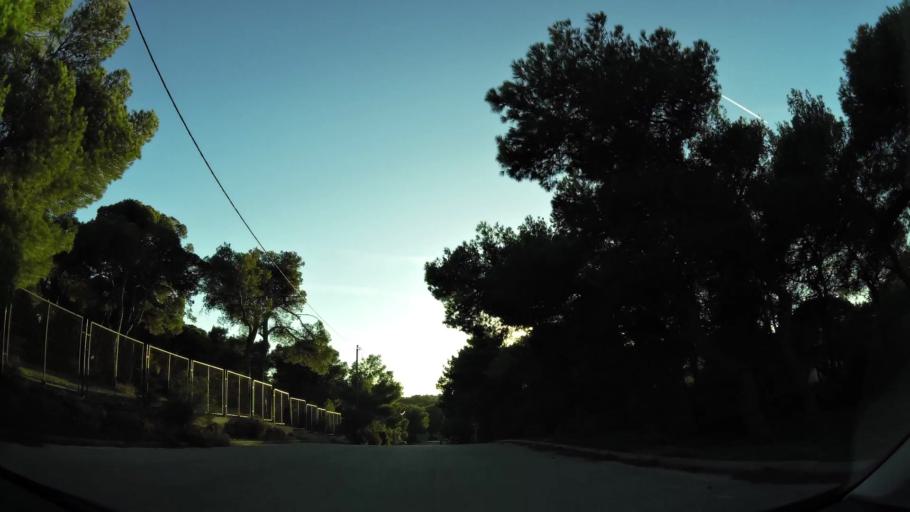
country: GR
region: Attica
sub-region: Nomarchia Anatolikis Attikis
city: Rafina
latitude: 38.0054
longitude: 24.0175
